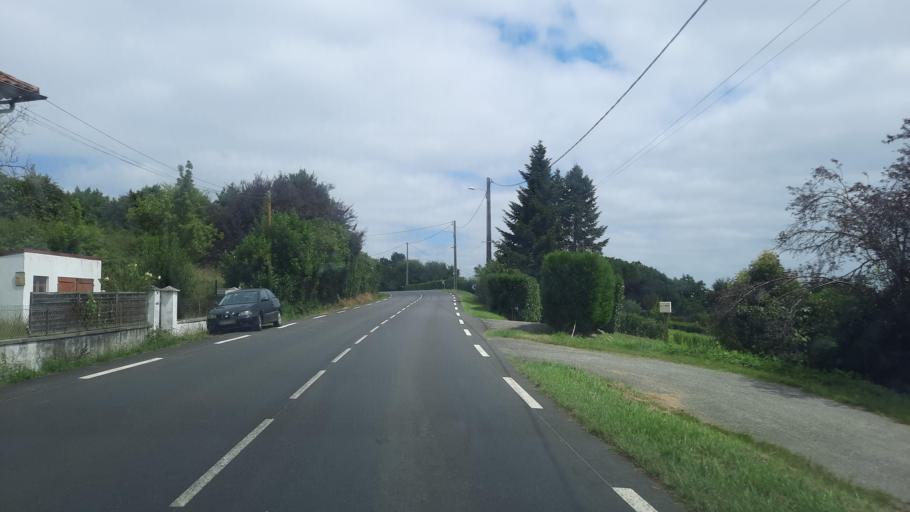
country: FR
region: Midi-Pyrenees
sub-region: Departement des Hautes-Pyrenees
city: Orleix
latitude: 43.2653
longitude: 0.1559
